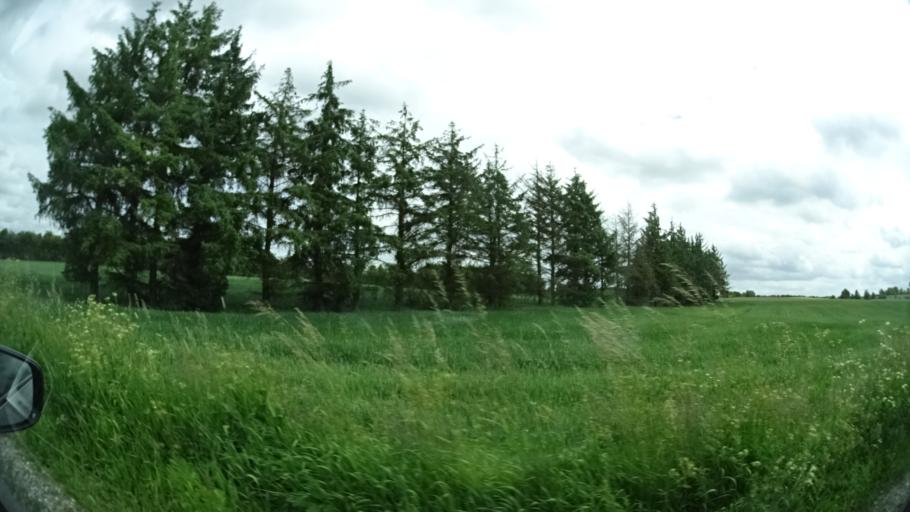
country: DK
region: Central Jutland
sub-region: Syddjurs Kommune
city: Ryomgard
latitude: 56.4285
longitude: 10.6143
